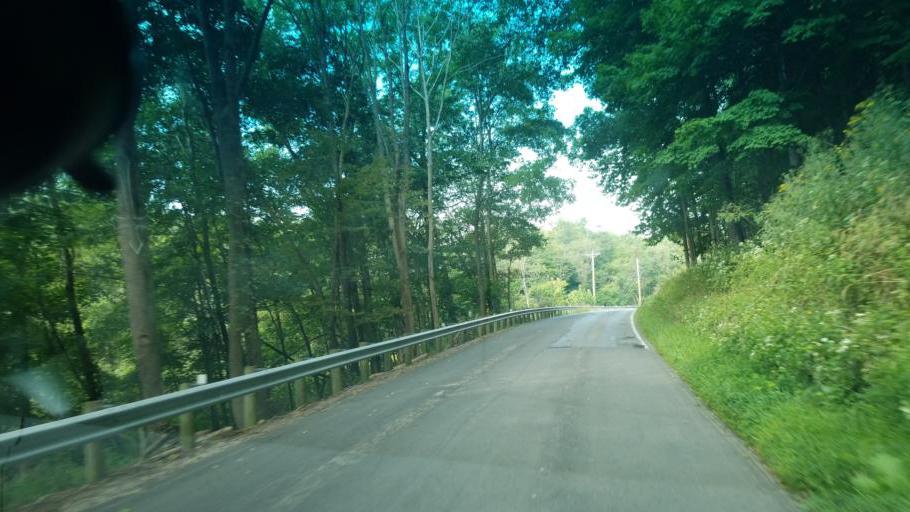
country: US
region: Ohio
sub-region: Licking County
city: Granville
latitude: 40.1231
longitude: -82.4991
